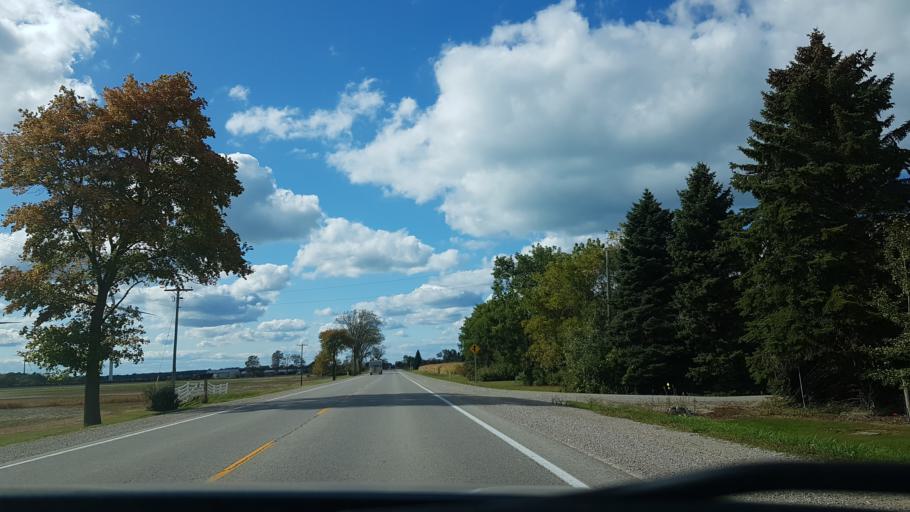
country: CA
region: Ontario
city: Bluewater
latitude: 43.3385
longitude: -81.7071
